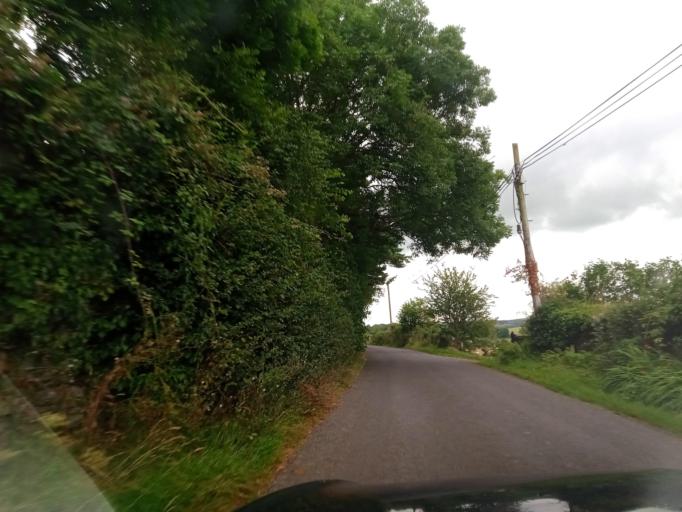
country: IE
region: Leinster
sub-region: Laois
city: Stradbally
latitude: 52.9709
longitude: -7.1500
